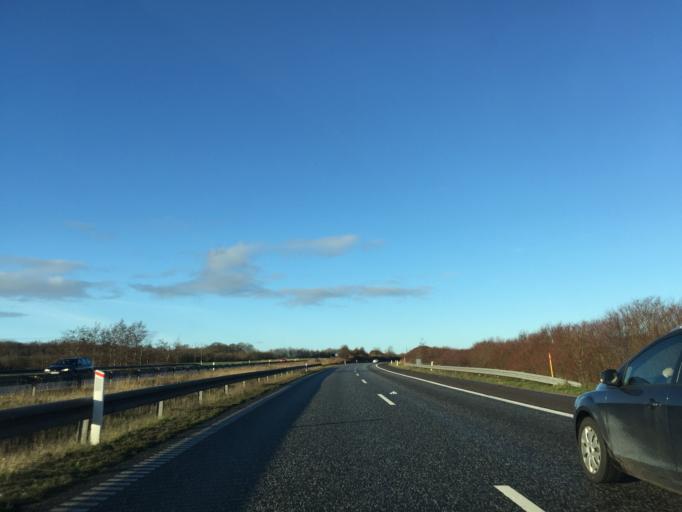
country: DK
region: South Denmark
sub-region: Fredericia Kommune
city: Taulov
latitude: 55.5949
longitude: 9.5936
